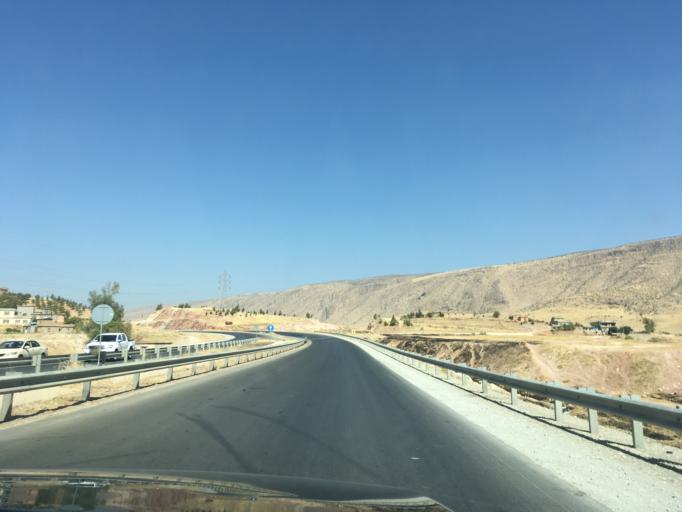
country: IQ
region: Arbil
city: Shaqlawah
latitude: 36.4840
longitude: 44.3813
